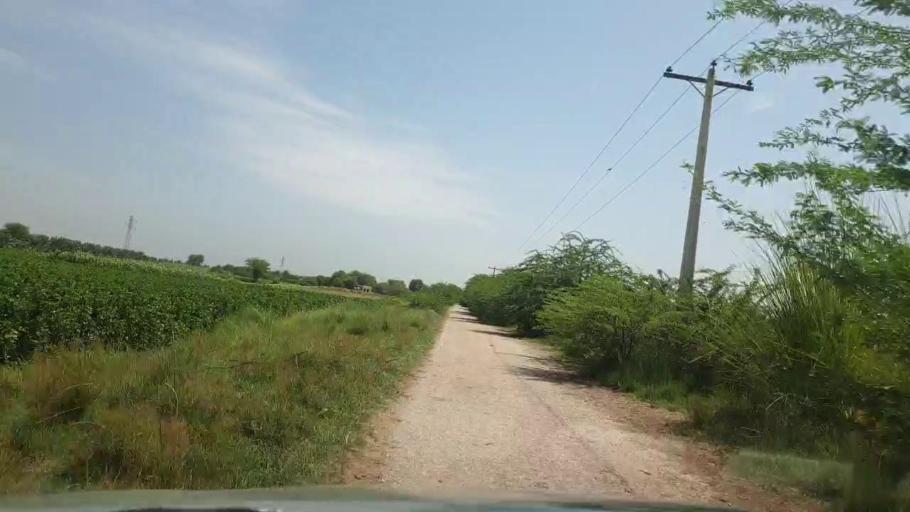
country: PK
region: Sindh
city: Bozdar
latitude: 27.1052
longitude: 68.9799
